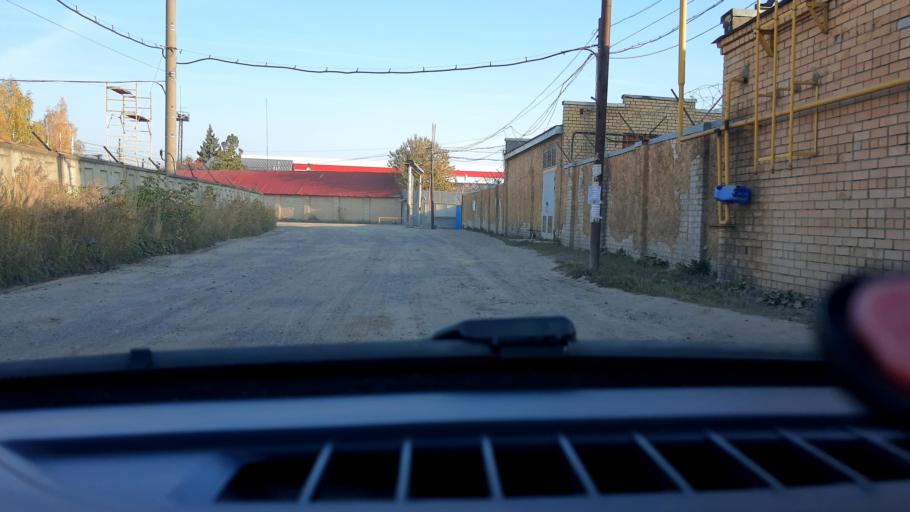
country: RU
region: Nizjnij Novgorod
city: Gorbatovka
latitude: 56.3069
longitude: 43.8291
